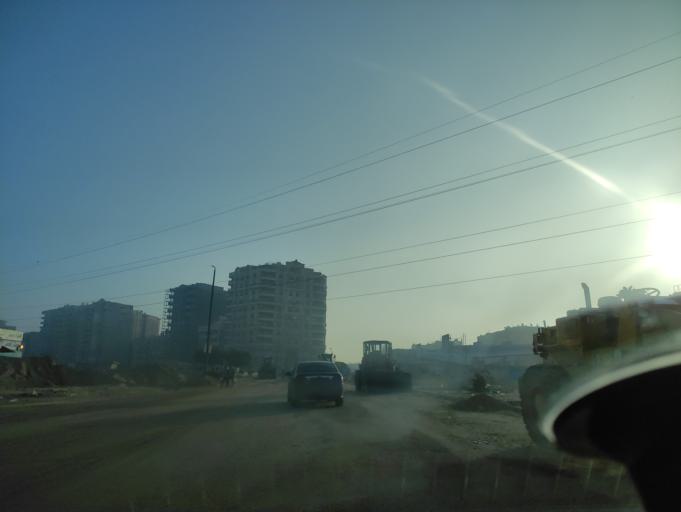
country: EG
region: Muhafazat al Qahirah
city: Cairo
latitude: 30.0480
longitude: 31.3656
